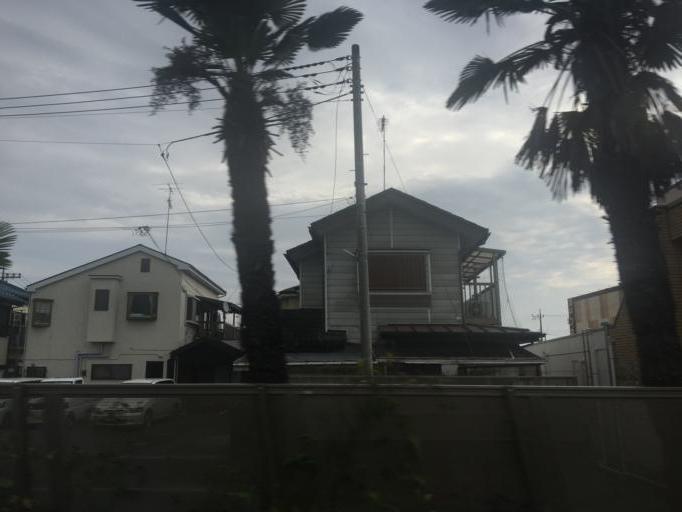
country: JP
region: Tokyo
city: Fussa
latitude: 35.7576
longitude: 139.3411
